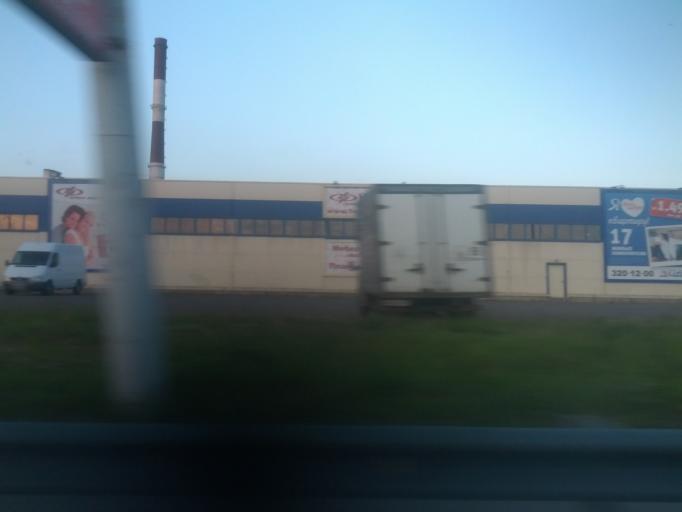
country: RU
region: St.-Petersburg
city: Staraya Derevnya
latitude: 59.9940
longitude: 30.2331
